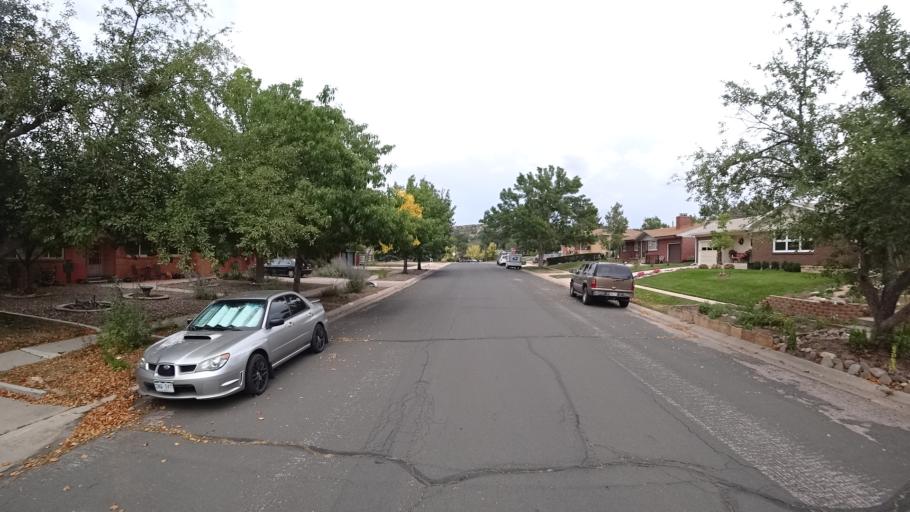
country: US
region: Colorado
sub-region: El Paso County
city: Colorado Springs
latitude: 38.8655
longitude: -104.7813
